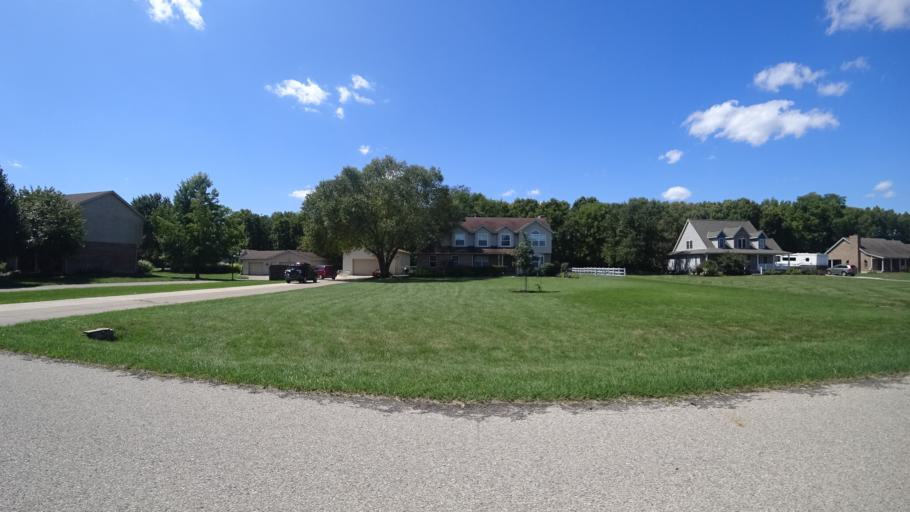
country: US
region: Ohio
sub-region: Butler County
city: New Miami
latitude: 39.4137
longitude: -84.5265
